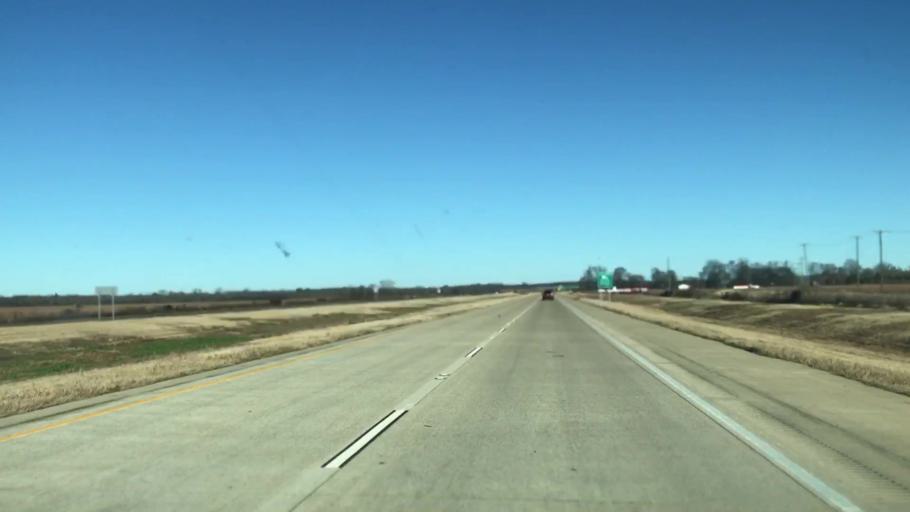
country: US
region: Louisiana
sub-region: Caddo Parish
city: Oil City
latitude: 32.7540
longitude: -93.8831
